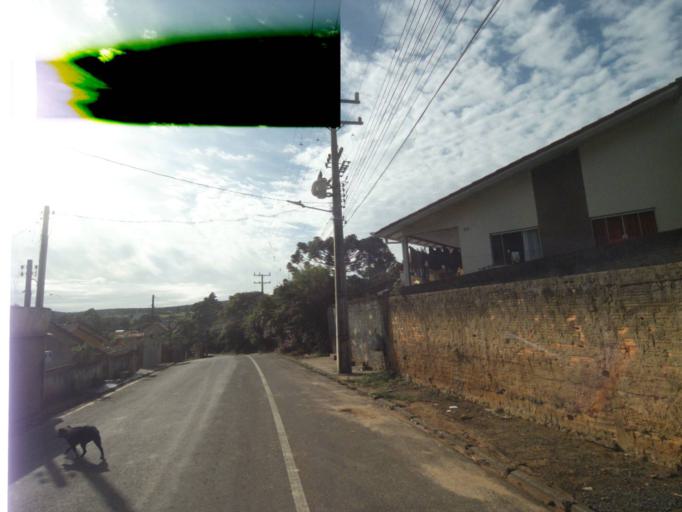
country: BR
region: Parana
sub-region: Telemaco Borba
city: Telemaco Borba
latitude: -24.3415
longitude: -50.6154
